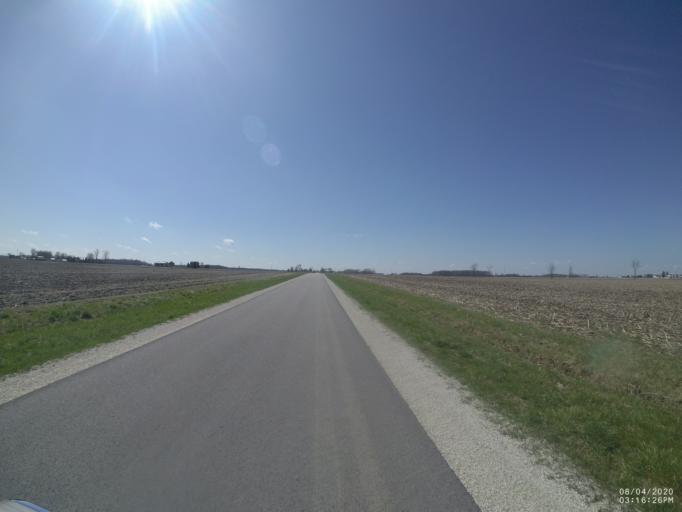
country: US
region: Ohio
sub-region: Sandusky County
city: Stony Prairie
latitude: 41.2820
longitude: -83.2305
